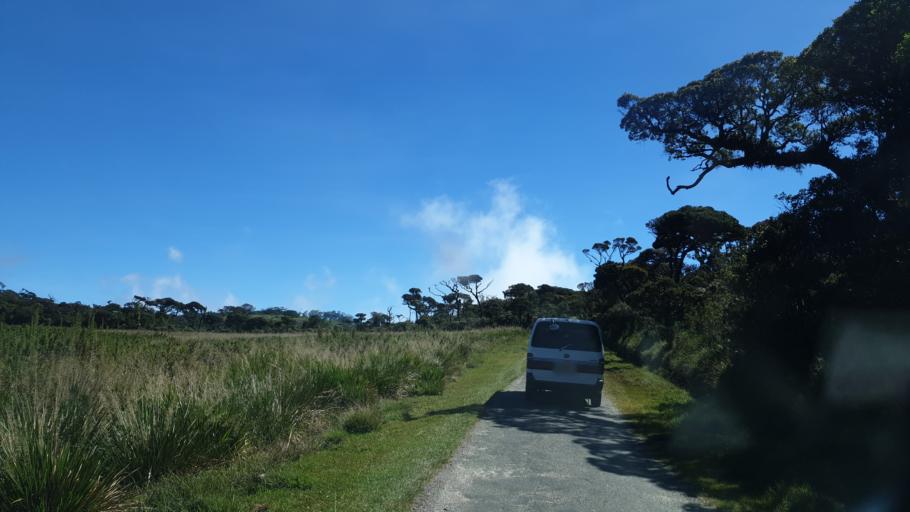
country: LK
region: Uva
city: Haputale
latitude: 6.7953
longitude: 80.8273
